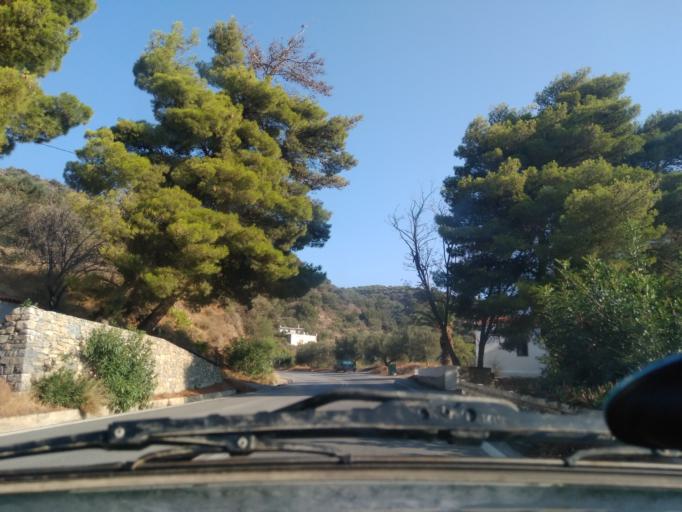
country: GR
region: Crete
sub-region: Nomos Lasithiou
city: Makry-Gialos
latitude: 35.1618
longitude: 25.9692
